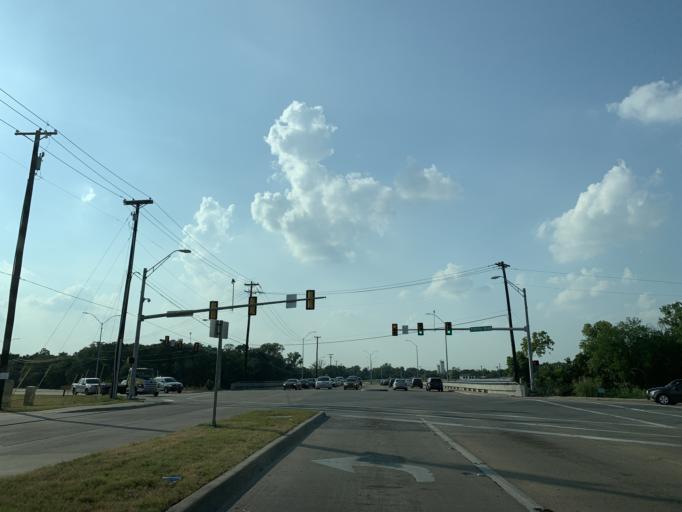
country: US
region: Texas
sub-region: Tarrant County
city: Hurst
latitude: 32.8021
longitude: -97.1832
